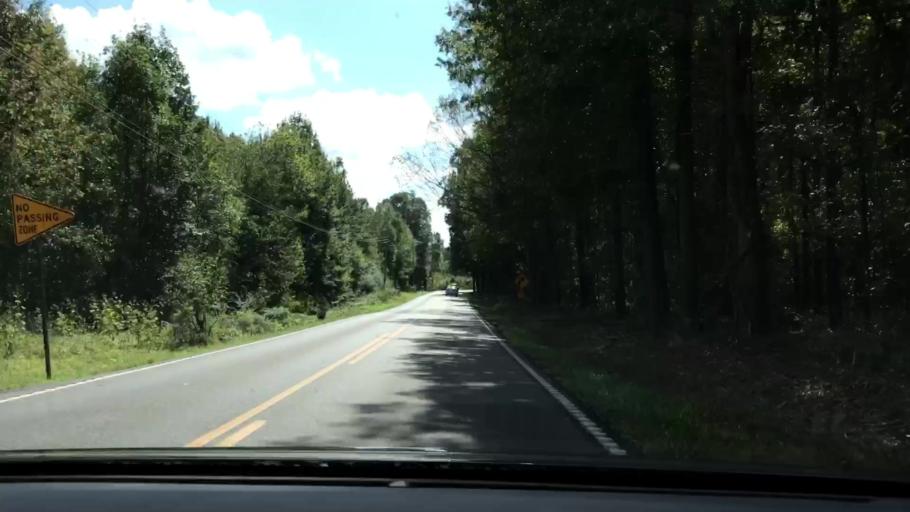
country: US
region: Kentucky
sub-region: McCracken County
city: Reidland
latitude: 36.9656
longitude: -88.5144
